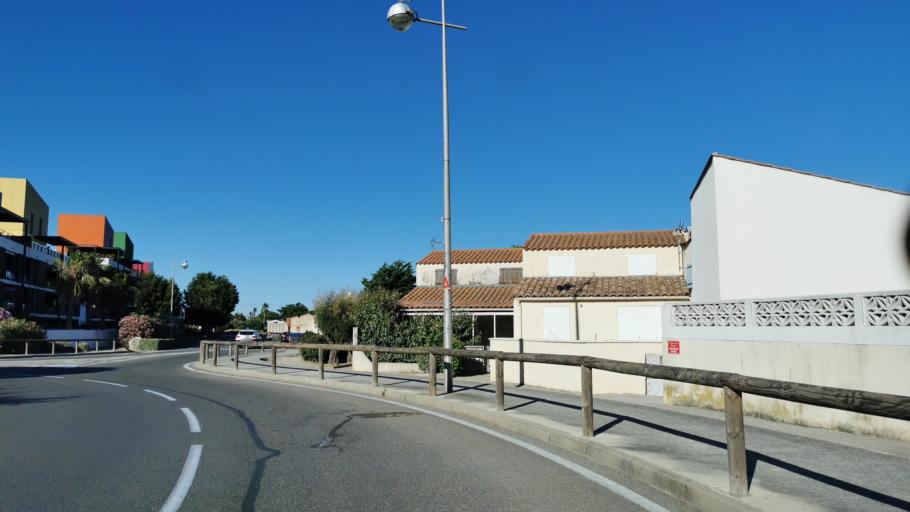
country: FR
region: Languedoc-Roussillon
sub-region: Departement de l'Aude
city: Gruissan
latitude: 43.1137
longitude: 3.1043
